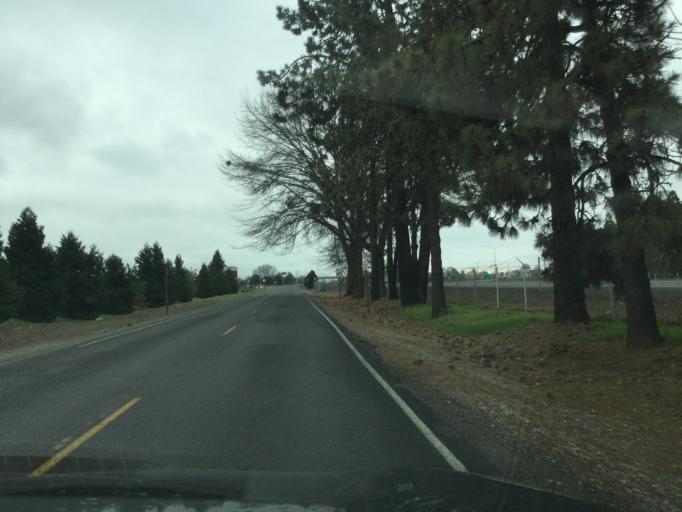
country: US
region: Oregon
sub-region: Jackson County
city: Central Point
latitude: 42.3829
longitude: -122.9093
